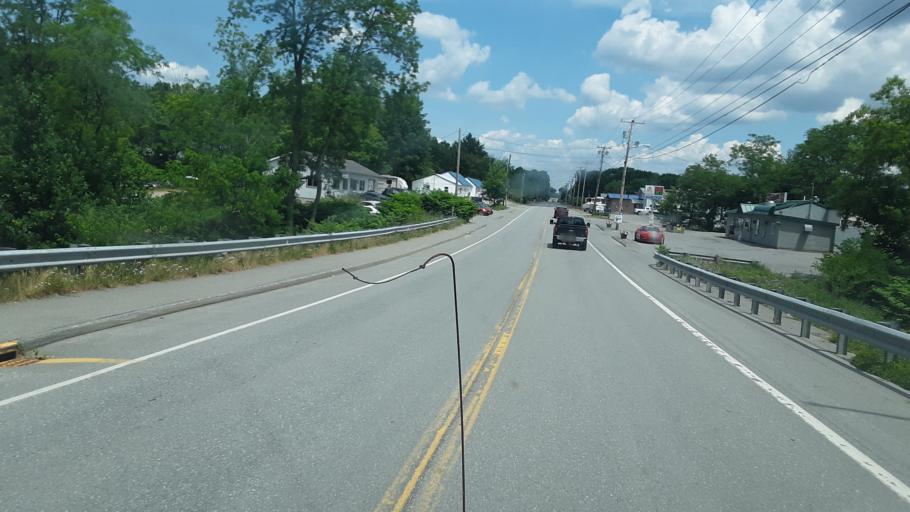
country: US
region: Maine
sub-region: Penobscot County
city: Hampden
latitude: 44.7658
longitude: -68.8011
